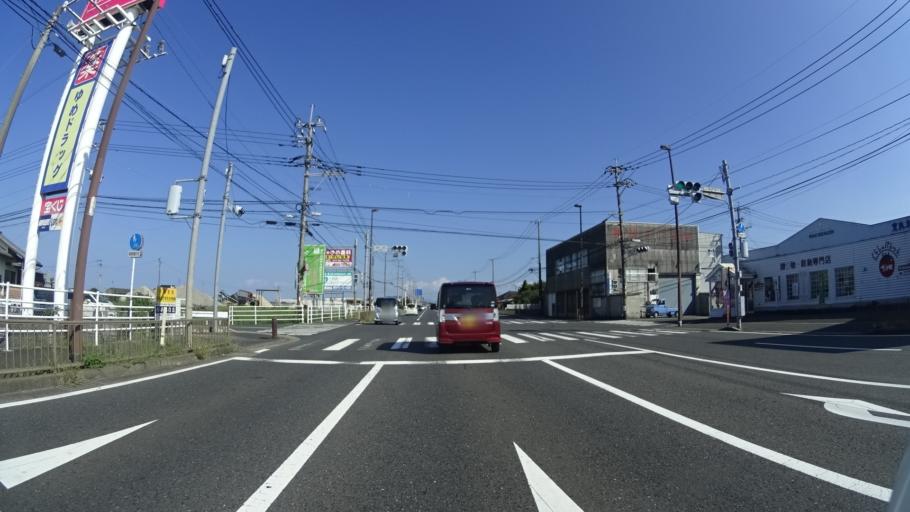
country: JP
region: Fukuoka
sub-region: Buzen-shi
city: Buzen
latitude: 33.5965
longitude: 131.1376
